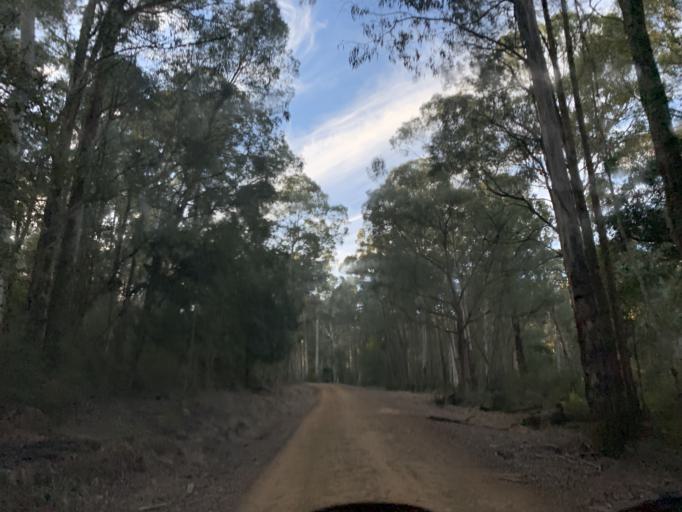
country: AU
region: Victoria
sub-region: Mansfield
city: Mansfield
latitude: -36.8893
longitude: 146.1209
